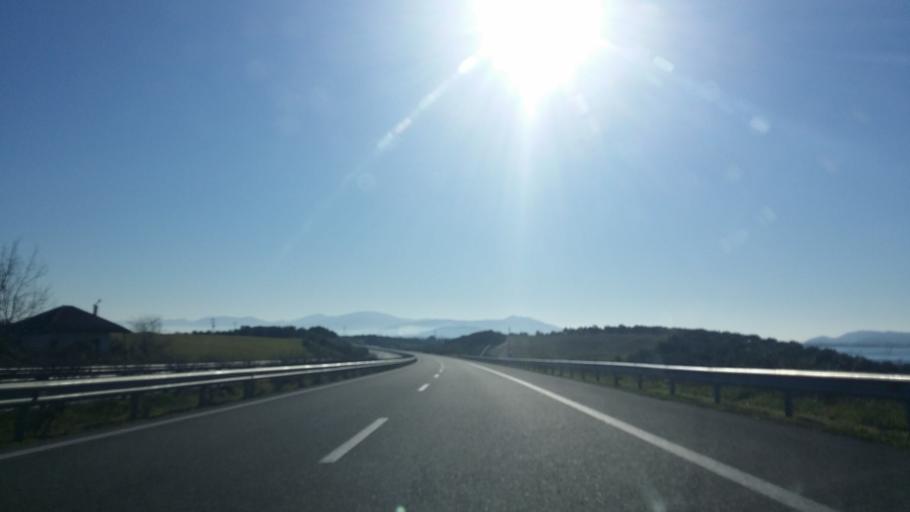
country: GR
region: West Greece
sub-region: Nomos Aitolias kai Akarnanias
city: Fitiai
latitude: 38.6788
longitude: 21.2201
